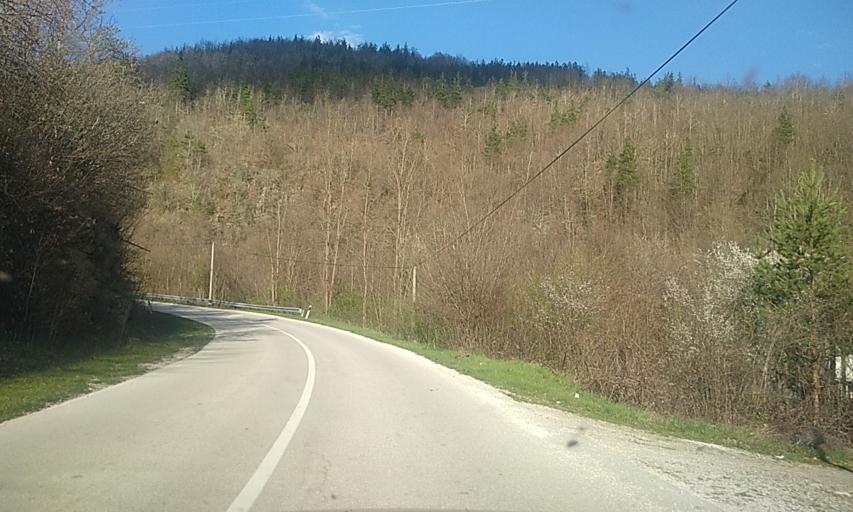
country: RS
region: Central Serbia
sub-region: Pcinjski Okrug
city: Bosilegrad
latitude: 42.4209
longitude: 22.5241
